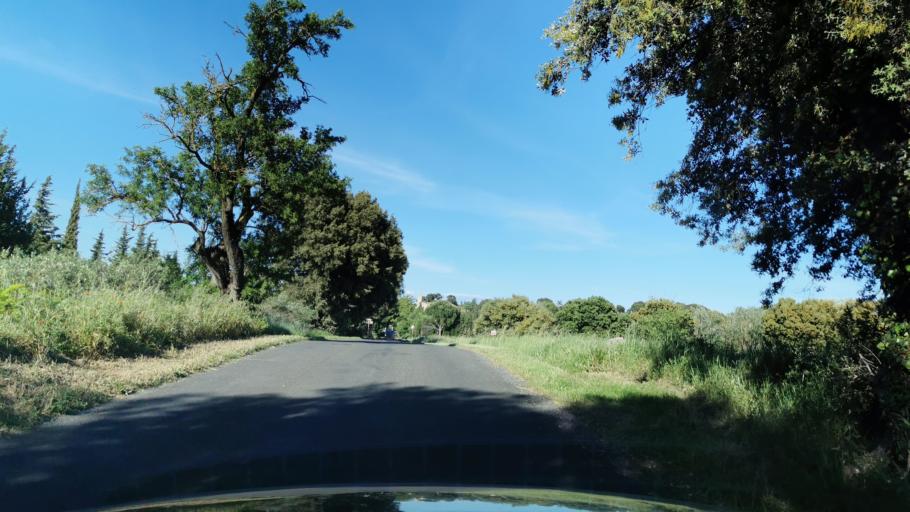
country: FR
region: Languedoc-Roussillon
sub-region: Departement de l'Aude
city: Marcorignan
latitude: 43.2225
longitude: 2.9152
